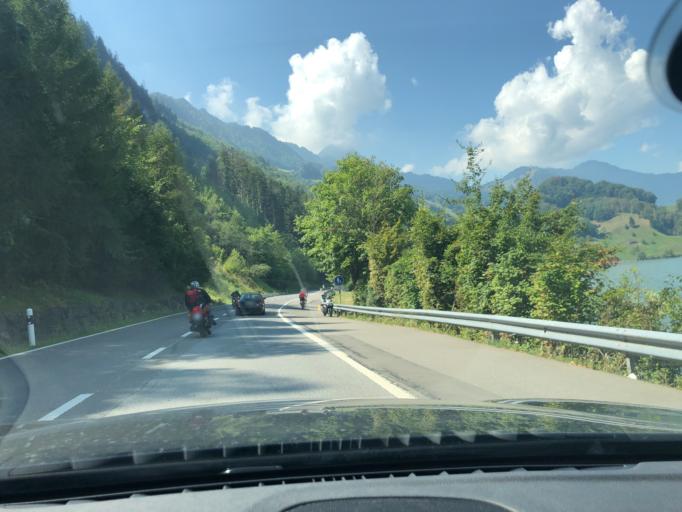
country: CH
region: Schwyz
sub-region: Bezirk Schwyz
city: Steinen
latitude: 47.0282
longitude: 8.6186
